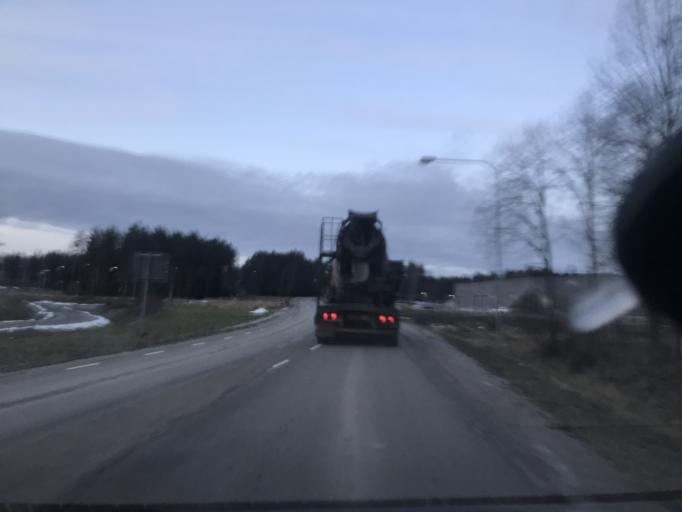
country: SE
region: Norrbotten
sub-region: Lulea Kommun
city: Bergnaset
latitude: 65.6156
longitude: 22.1229
